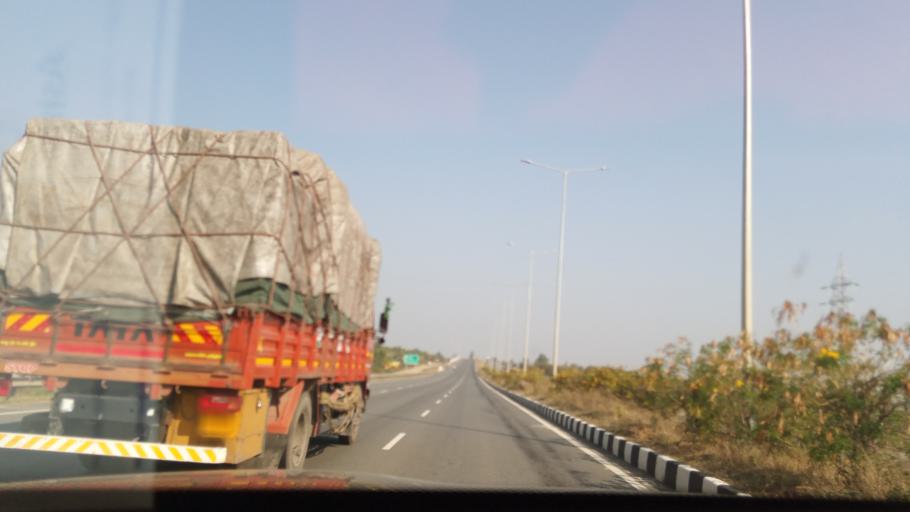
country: IN
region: Karnataka
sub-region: Haveri
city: Savanur
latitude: 14.8663
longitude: 75.3208
